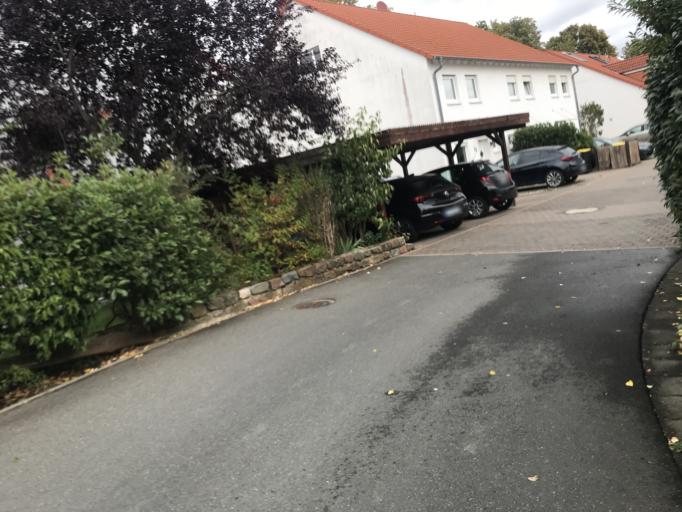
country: DE
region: Rheinland-Pfalz
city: Jugenheim
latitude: 49.8941
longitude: 8.0784
